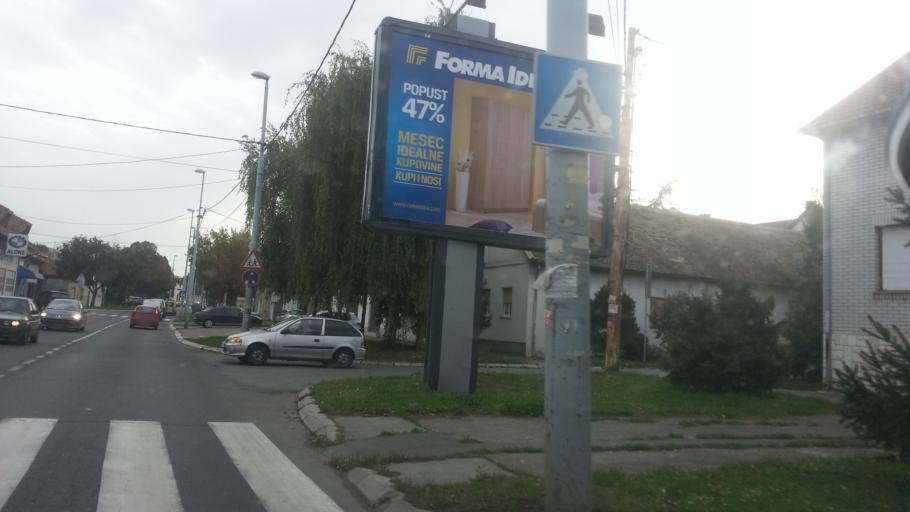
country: RS
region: Central Serbia
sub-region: Belgrade
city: Zemun
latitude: 44.8497
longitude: 20.3891
